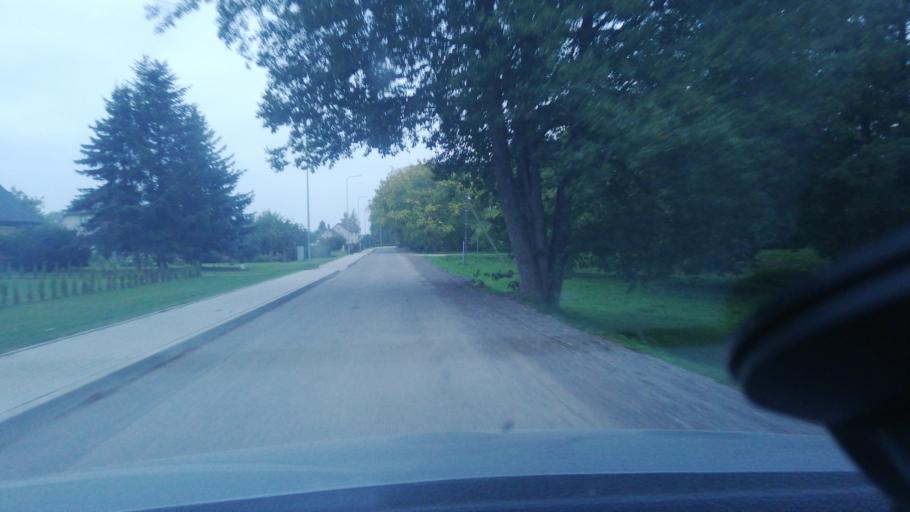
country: LT
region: Klaipedos apskritis
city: Kretinga
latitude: 55.9399
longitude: 21.1829
